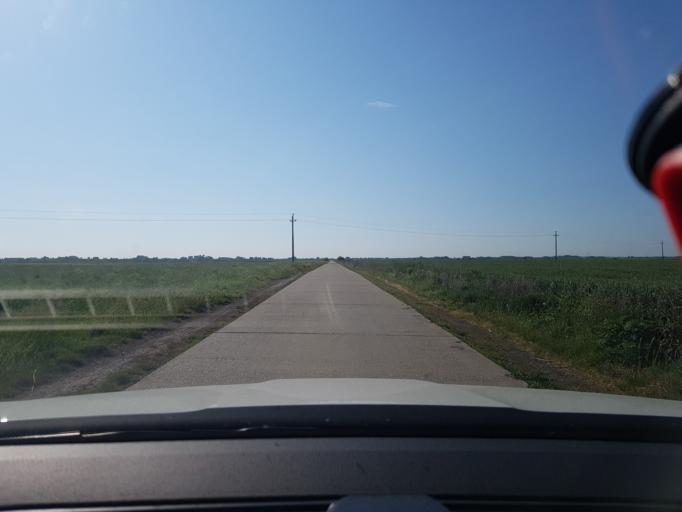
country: HU
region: Tolna
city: Decs
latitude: 46.2831
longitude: 18.6989
